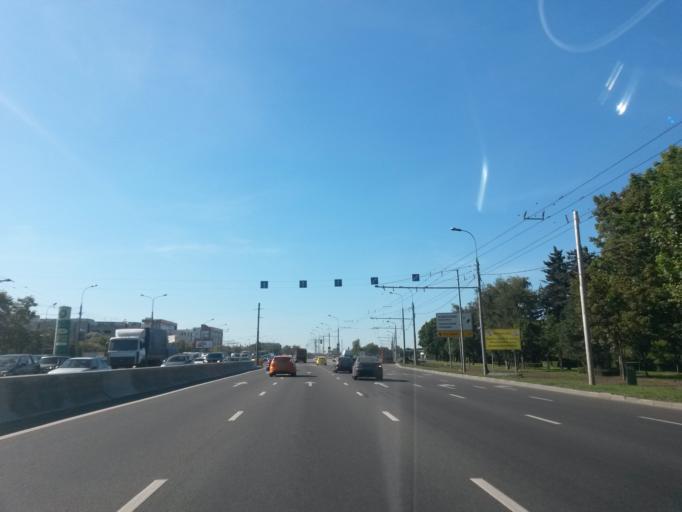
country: RU
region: Moscow
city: Tsaritsyno
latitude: 55.6503
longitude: 37.6603
